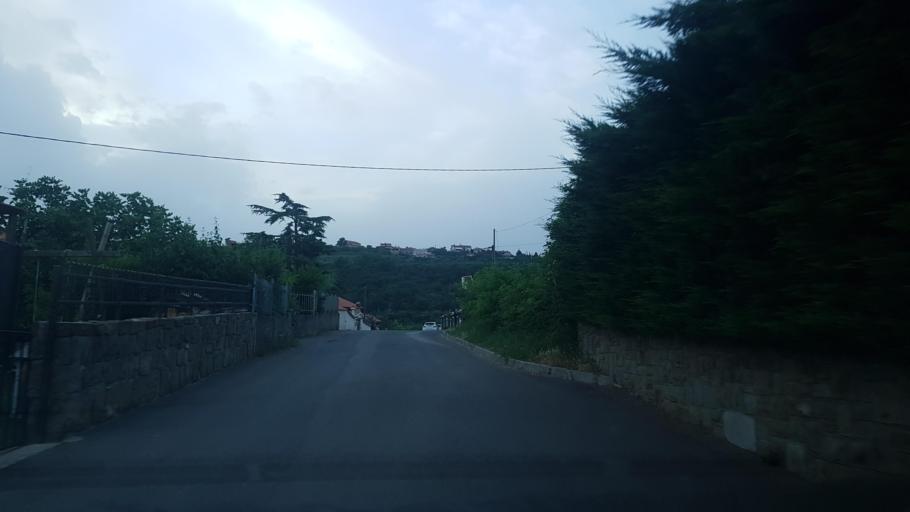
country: SI
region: Koper-Capodistria
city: Spodnje Skofije
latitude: 45.5735
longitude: 13.7877
